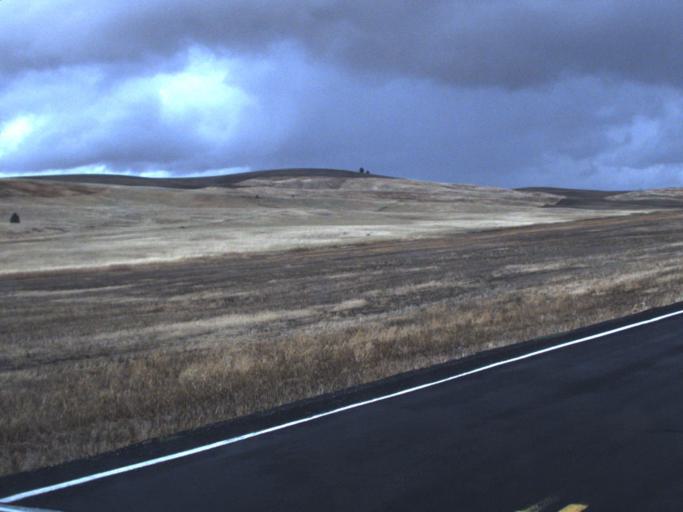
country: US
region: Washington
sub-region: Spokane County
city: Medical Lake
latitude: 47.6929
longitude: -117.8815
